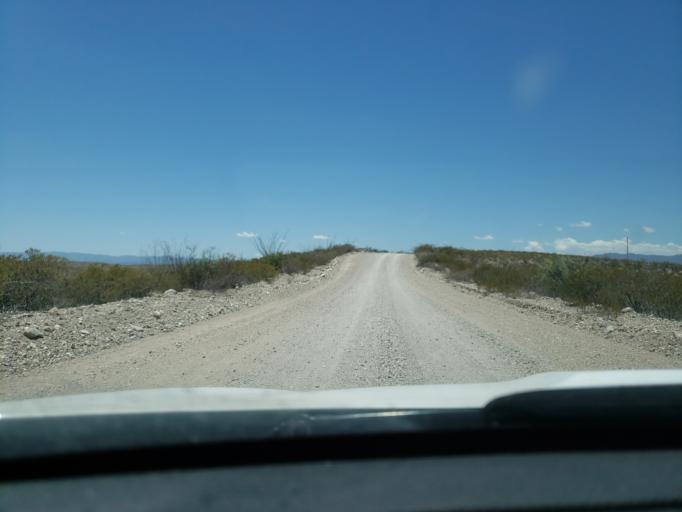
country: MX
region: Chihuahua
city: Ojinaga
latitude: 29.9977
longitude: -104.5767
